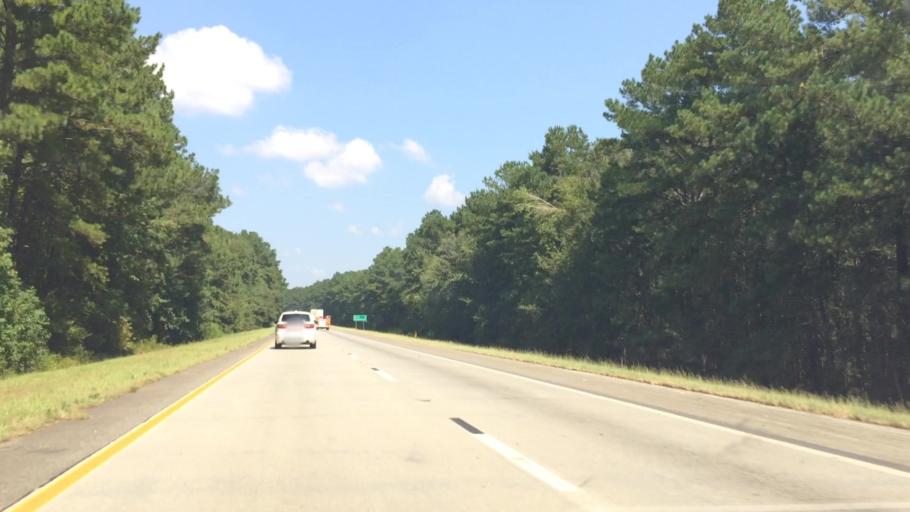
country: US
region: South Carolina
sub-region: Colleton County
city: Walterboro
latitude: 33.0149
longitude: -80.6663
